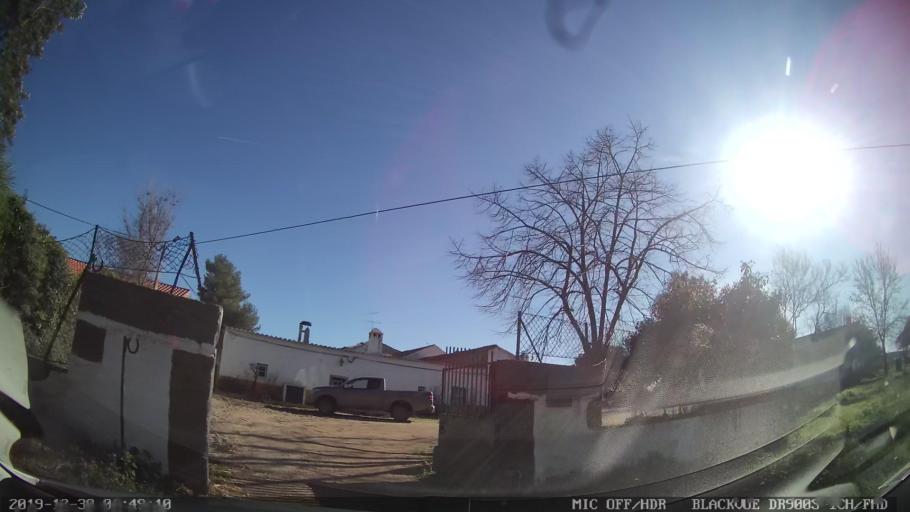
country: PT
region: Castelo Branco
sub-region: Idanha-A-Nova
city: Idanha-a-Nova
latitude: 39.8628
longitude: -7.1337
